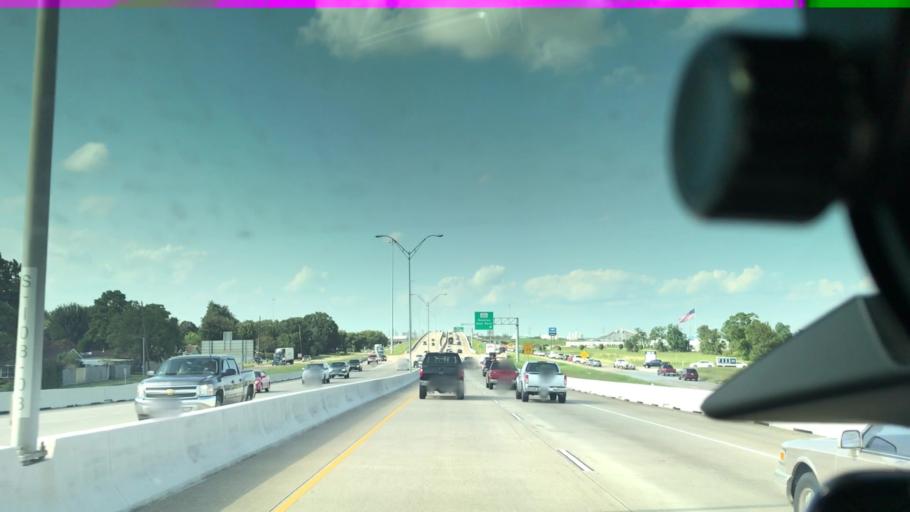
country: US
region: Texas
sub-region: Harris County
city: Deer Park
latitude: 29.7040
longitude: -95.1534
